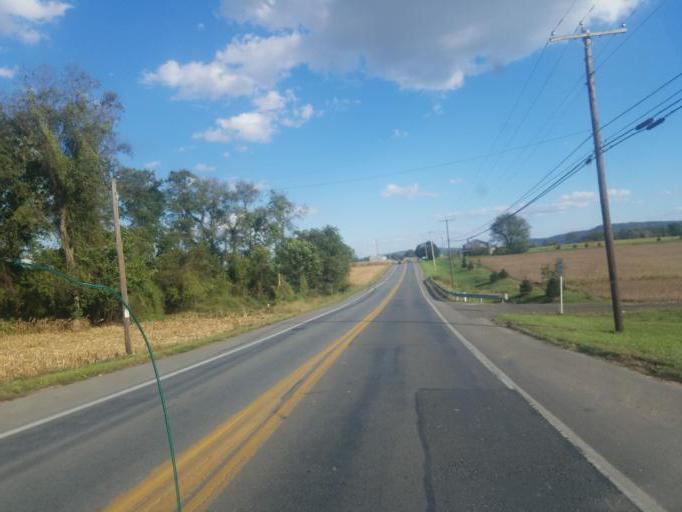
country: US
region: Pennsylvania
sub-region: Lancaster County
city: Bainbridge
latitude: 40.0736
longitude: -76.6386
